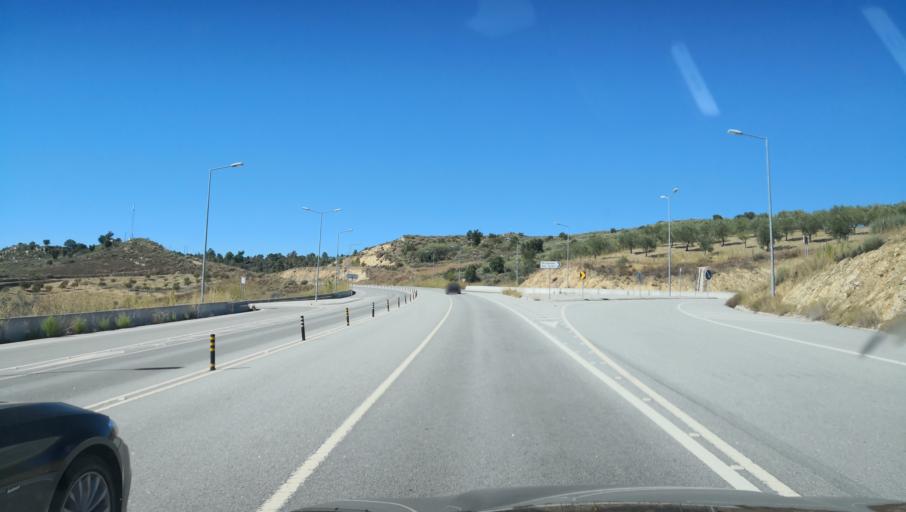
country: PT
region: Vila Real
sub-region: Valpacos
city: Valpacos
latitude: 41.5649
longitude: -7.2702
